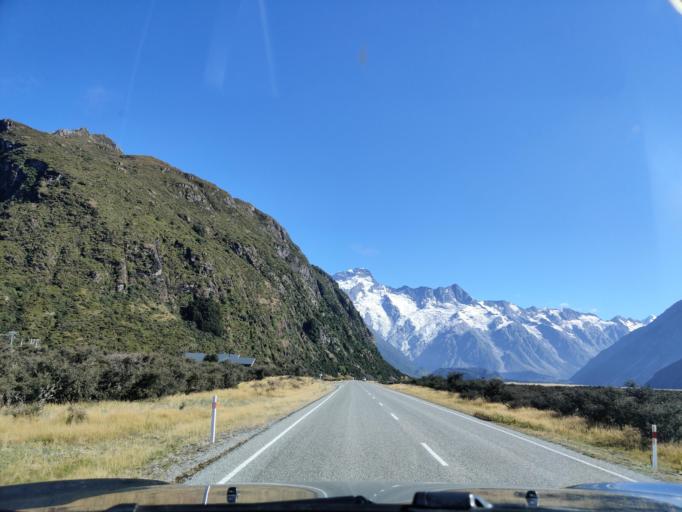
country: NZ
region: Canterbury
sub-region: Timaru District
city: Pleasant Point
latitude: -43.7597
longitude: 170.1201
